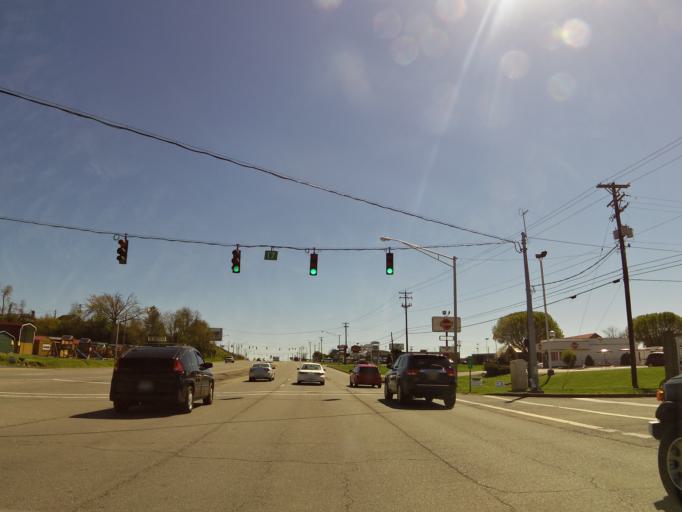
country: US
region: Kentucky
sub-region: Pulaski County
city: Somerset
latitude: 37.0555
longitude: -84.6247
